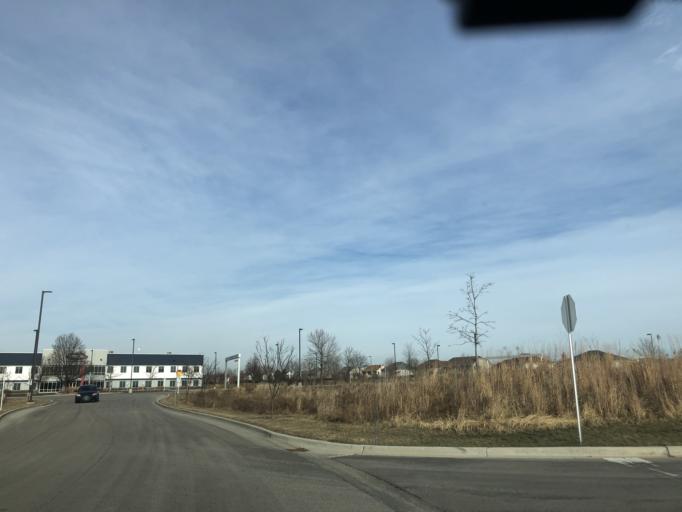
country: US
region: Illinois
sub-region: DuPage County
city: Woodridge
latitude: 41.7130
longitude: -88.0284
